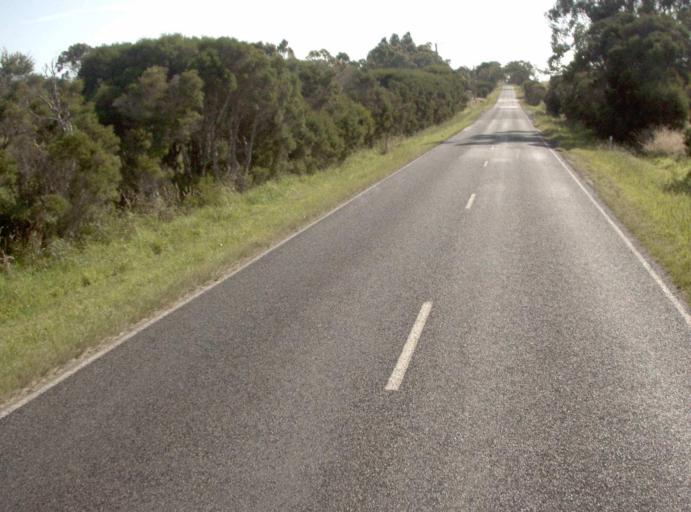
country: AU
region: Victoria
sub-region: Baw Baw
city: Warragul
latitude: -38.5544
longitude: 146.0497
